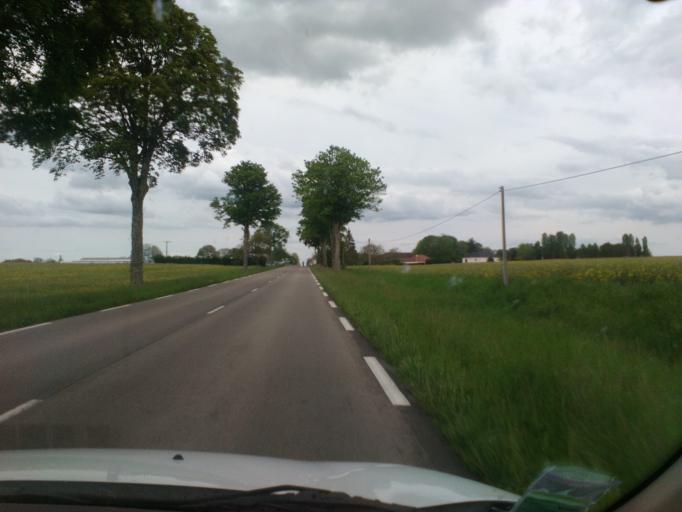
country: FR
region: Champagne-Ardenne
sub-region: Departement de l'Aube
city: Vendeuvre-sur-Barse
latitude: 48.2386
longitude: 4.5272
